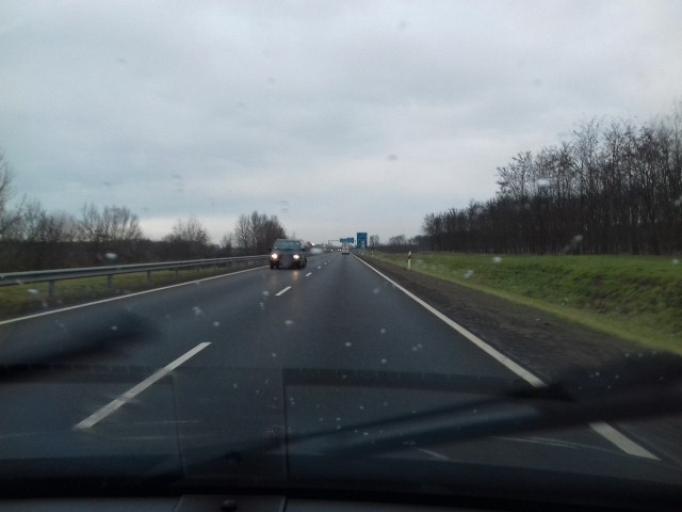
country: HU
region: Szabolcs-Szatmar-Bereg
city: Nagykallo
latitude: 47.9058
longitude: 21.8178
